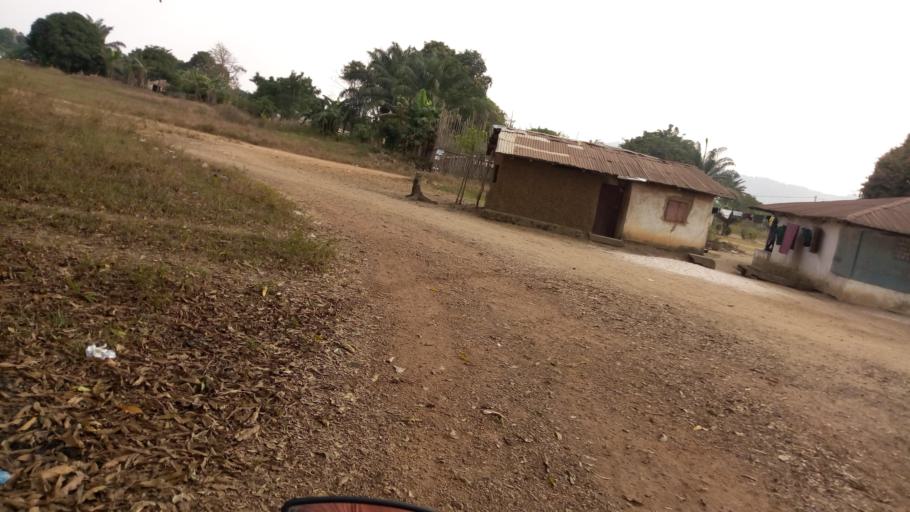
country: SL
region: Southern Province
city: Mogbwemo
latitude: 7.7637
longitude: -12.3128
